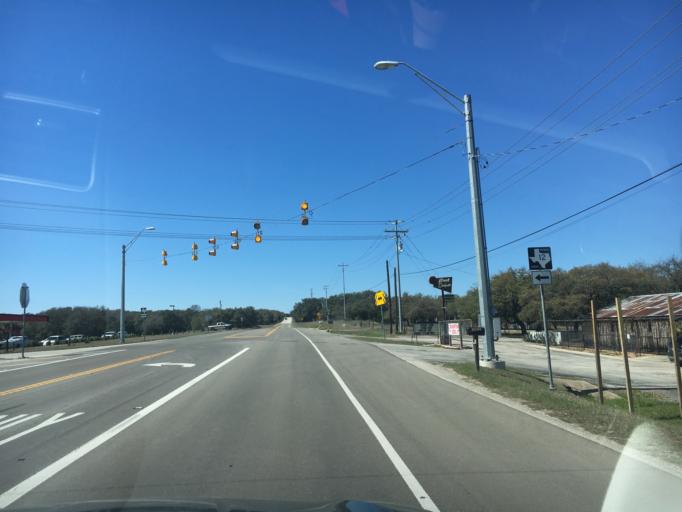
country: US
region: Texas
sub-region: Hays County
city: Dripping Springs
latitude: 30.2864
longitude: -98.0644
